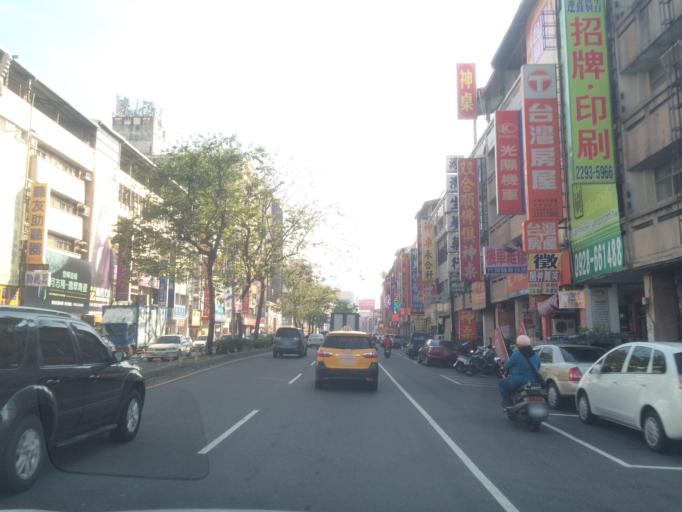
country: TW
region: Taiwan
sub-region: Taichung City
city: Taichung
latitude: 24.1734
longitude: 120.6714
